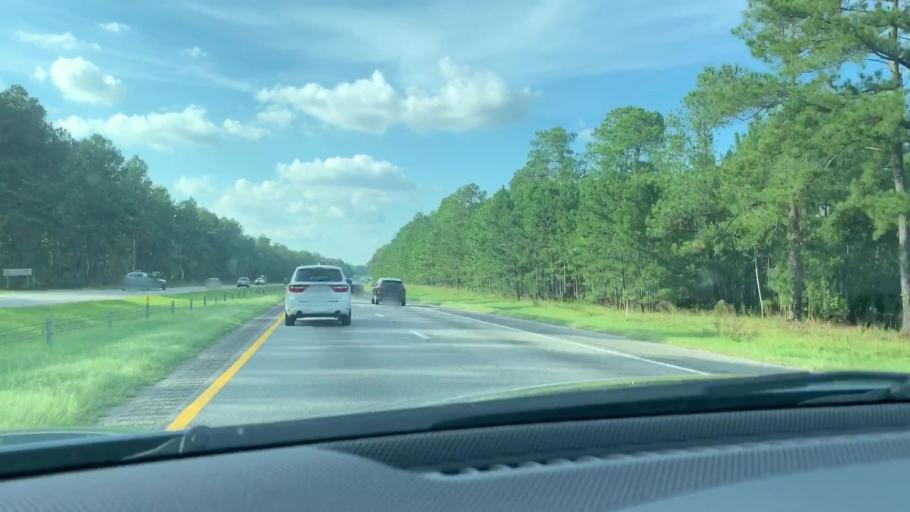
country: US
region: South Carolina
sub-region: Orangeburg County
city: Brookdale
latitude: 33.5249
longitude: -80.7960
